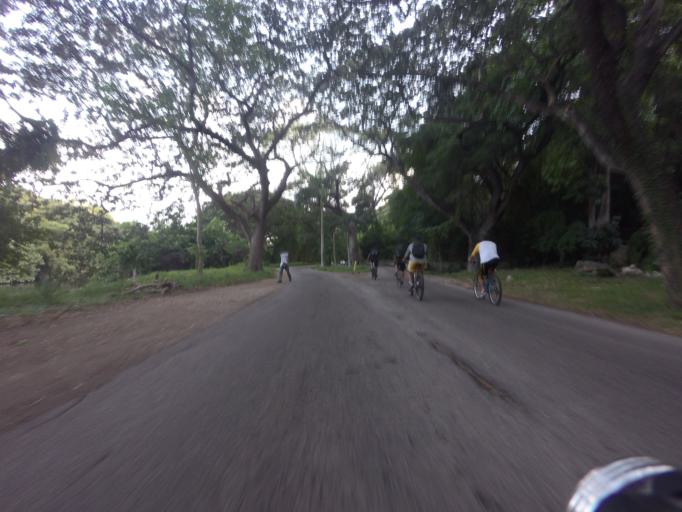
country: CU
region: La Habana
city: Cerro
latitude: 23.1142
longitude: -82.4068
